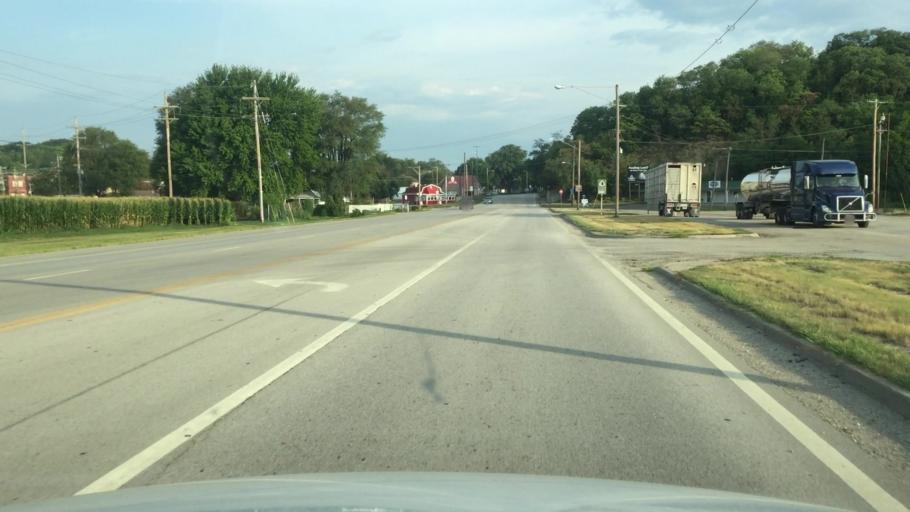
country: US
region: Kansas
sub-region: Doniphan County
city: Wathena
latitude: 39.7589
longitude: -94.9435
